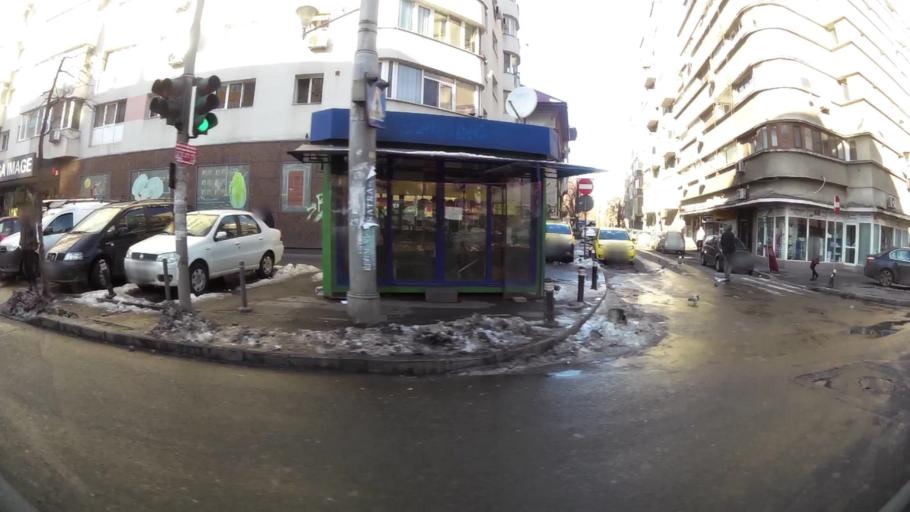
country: RO
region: Bucuresti
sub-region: Municipiul Bucuresti
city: Bucharest
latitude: 44.4473
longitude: 26.1226
